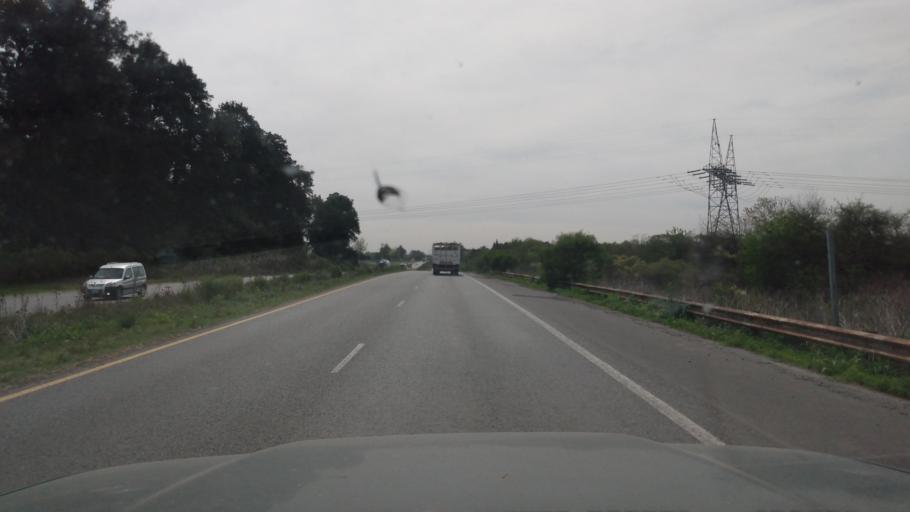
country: AR
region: Buenos Aires
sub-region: Partido de Lujan
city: Lujan
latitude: -34.4536
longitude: -59.0557
